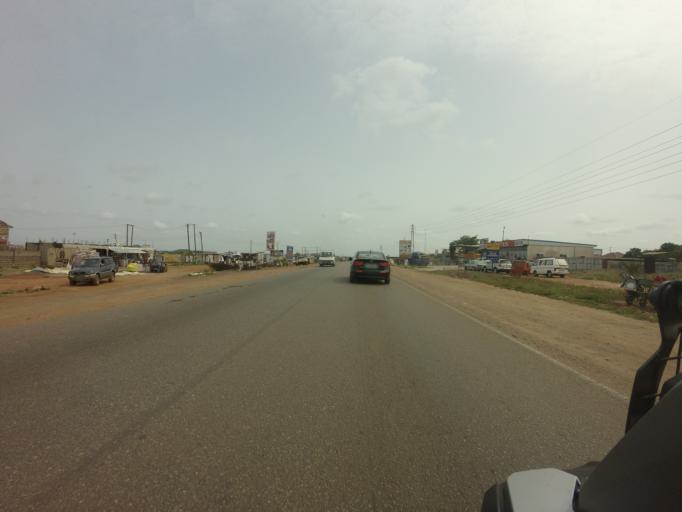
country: GH
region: Greater Accra
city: Tema
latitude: 5.7391
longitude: 0.0337
